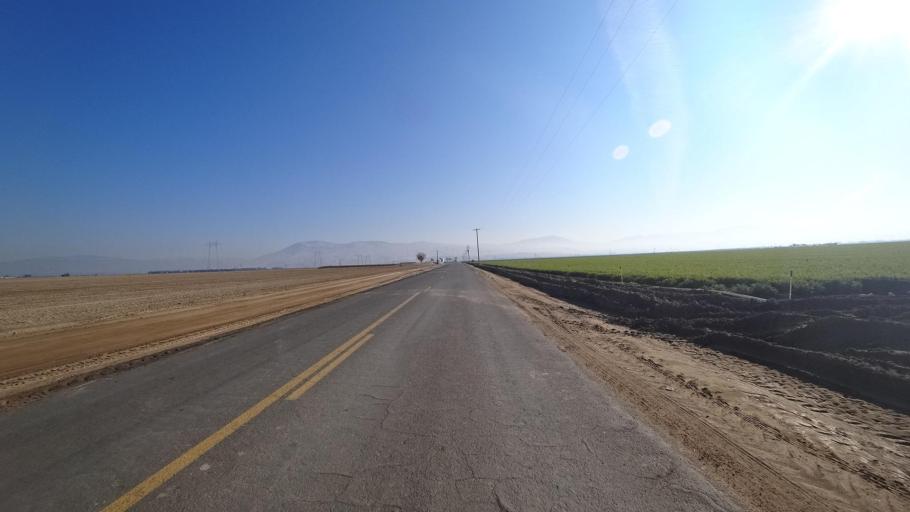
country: US
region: California
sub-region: Kern County
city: Weedpatch
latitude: 35.1220
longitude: -118.9138
